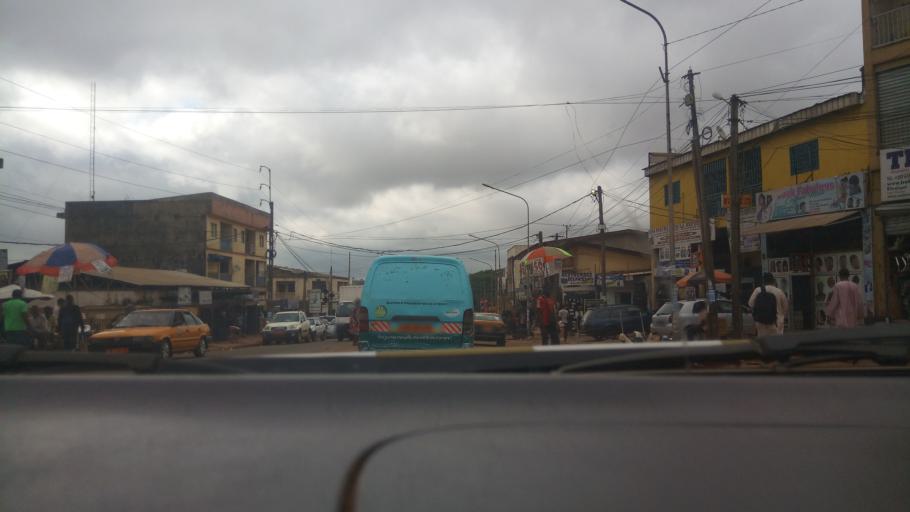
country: CM
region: Centre
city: Yaounde
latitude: 3.8799
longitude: 11.5078
